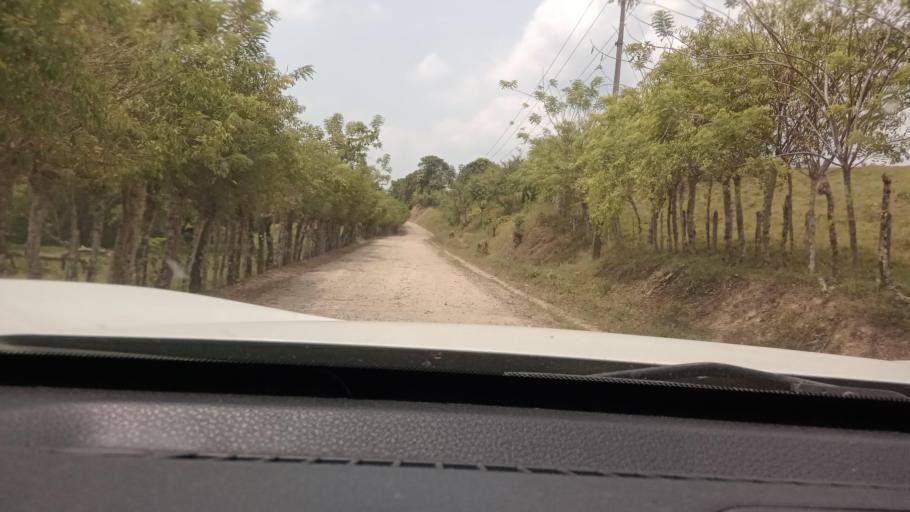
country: MX
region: Tabasco
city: Chontalpa
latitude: 17.5685
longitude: -93.7122
